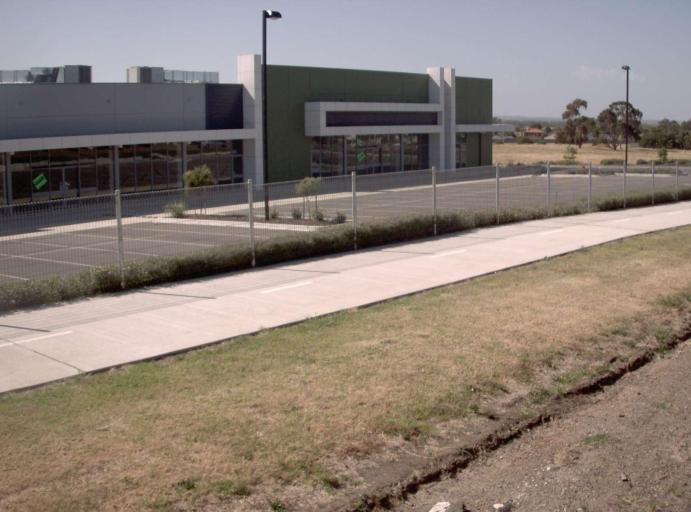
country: AU
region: Victoria
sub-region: Frankston
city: Carrum Downs
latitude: -38.0977
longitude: 145.1739
